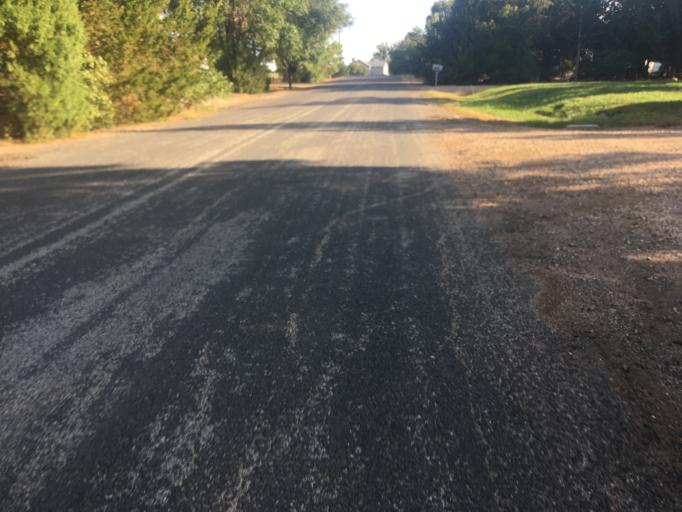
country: US
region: Colorado
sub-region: Boulder County
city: Louisville
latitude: 39.9954
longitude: -105.1258
